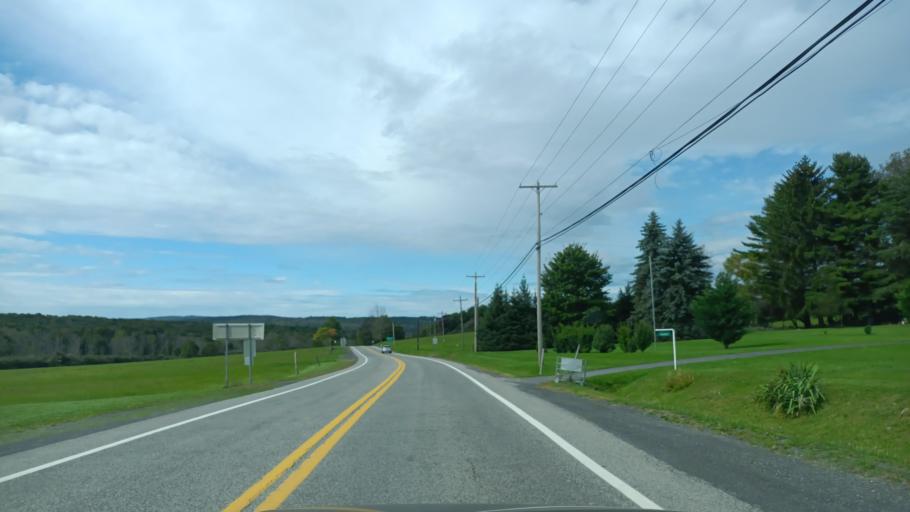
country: US
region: Maryland
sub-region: Garrett County
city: Mountain Lake Park
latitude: 39.2768
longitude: -79.2419
